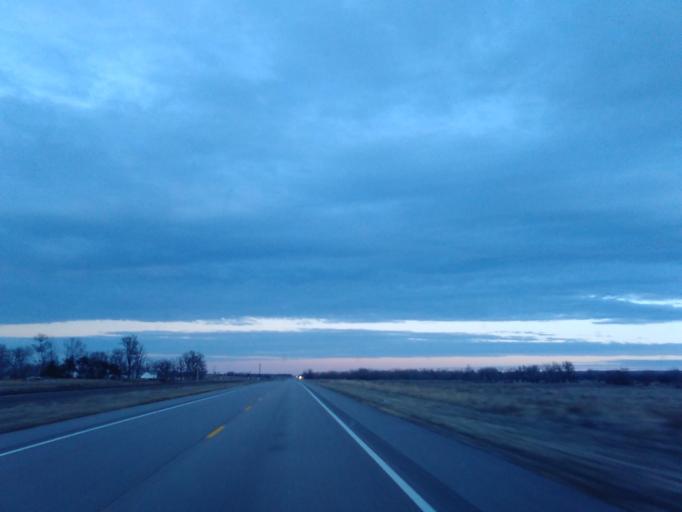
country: US
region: Nebraska
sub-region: Garden County
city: Oshkosh
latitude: 41.3673
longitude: -102.2354
